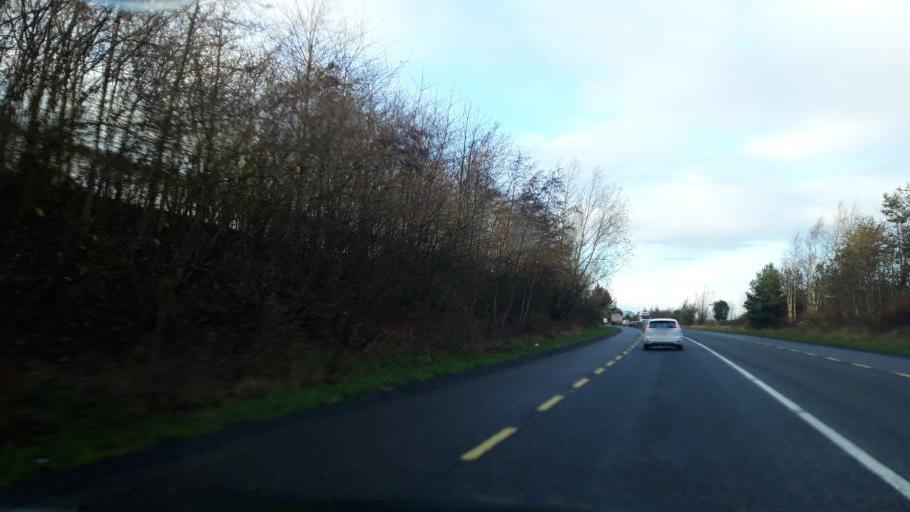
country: IE
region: Ulster
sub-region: County Monaghan
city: Carrickmacross
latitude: 53.9535
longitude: -6.6737
